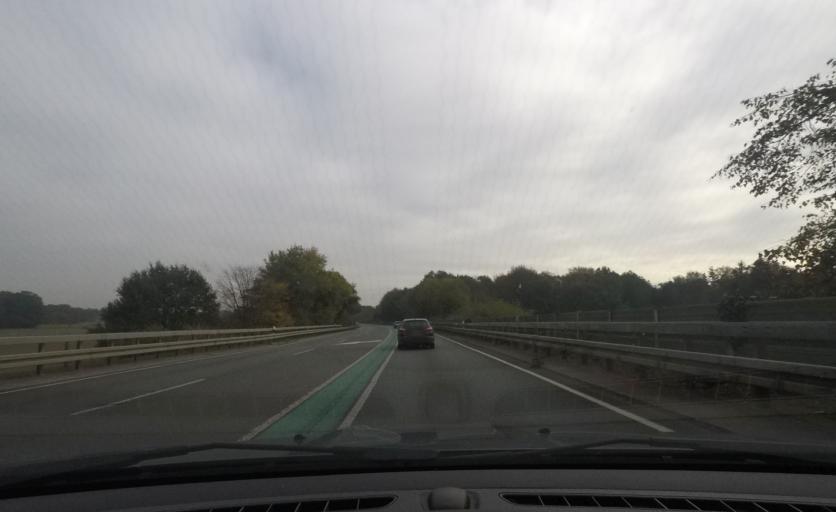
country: DE
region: North Rhine-Westphalia
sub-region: Regierungsbezirk Munster
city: Borken
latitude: 51.8299
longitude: 6.8593
